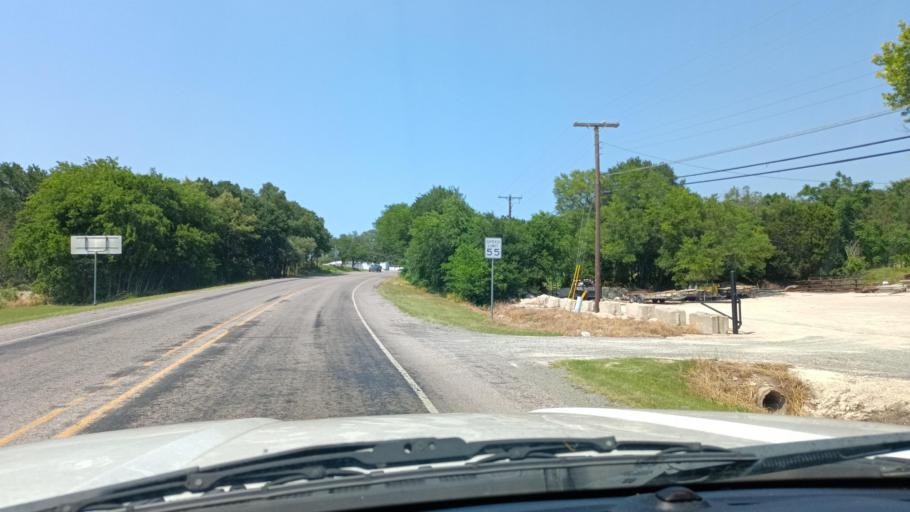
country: US
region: Texas
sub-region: Bell County
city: Belton
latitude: 31.1005
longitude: -97.5163
